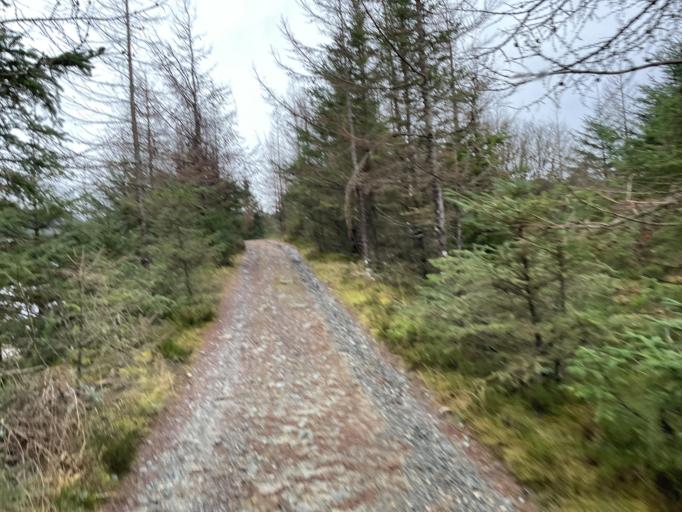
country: GB
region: Scotland
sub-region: Highland
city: Fort William
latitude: 56.8128
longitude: -5.0949
